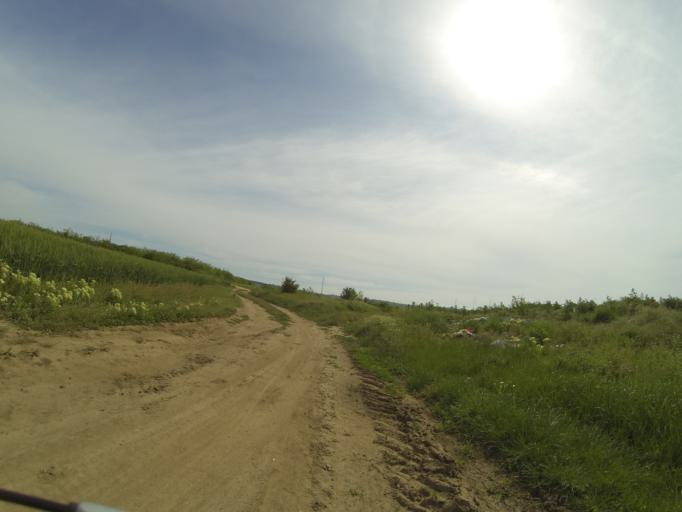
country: RO
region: Dolj
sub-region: Comuna Malu Mare
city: Preajba
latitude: 44.2677
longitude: 23.8627
